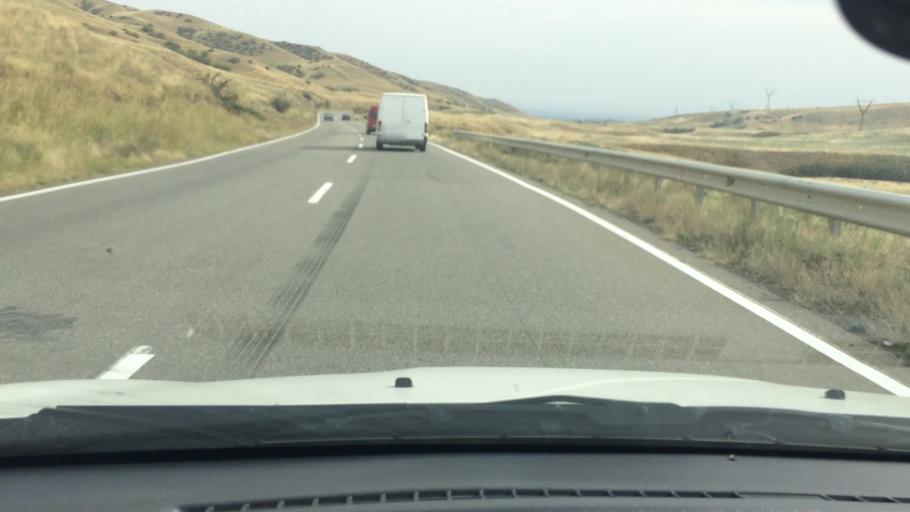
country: GE
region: Kvemo Kartli
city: Rust'avi
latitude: 41.4999
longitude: 44.9574
